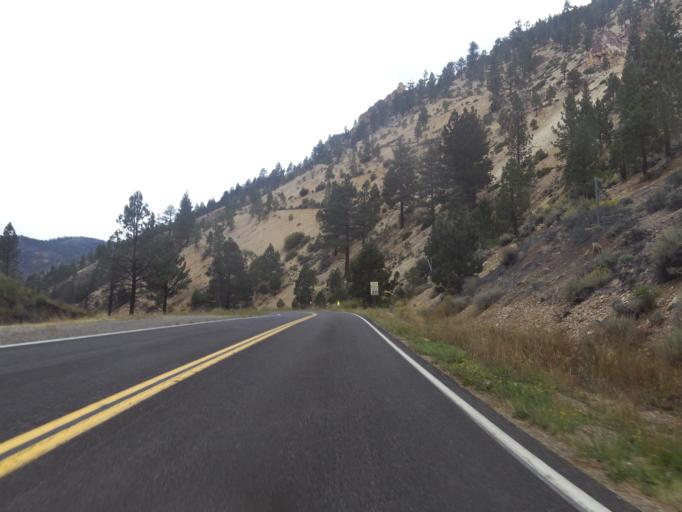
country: US
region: Nevada
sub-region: Douglas County
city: Gardnerville Ranchos
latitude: 38.6657
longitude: -119.7038
